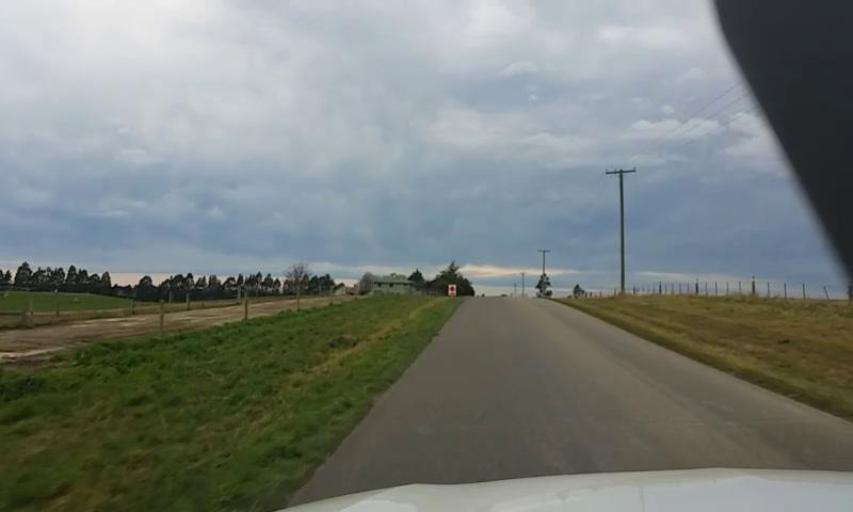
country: NZ
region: Canterbury
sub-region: Waimakariri District
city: Kaiapoi
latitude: -43.2981
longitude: 172.4794
